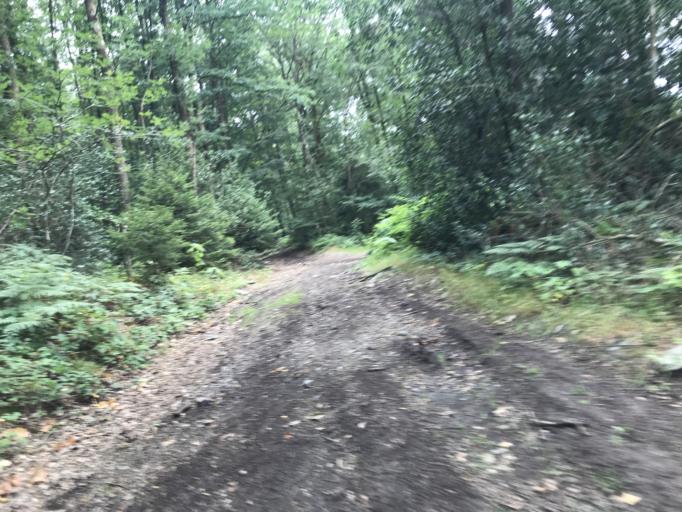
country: FR
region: Champagne-Ardenne
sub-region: Departement des Ardennes
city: Montherme
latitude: 49.8925
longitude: 4.7482
